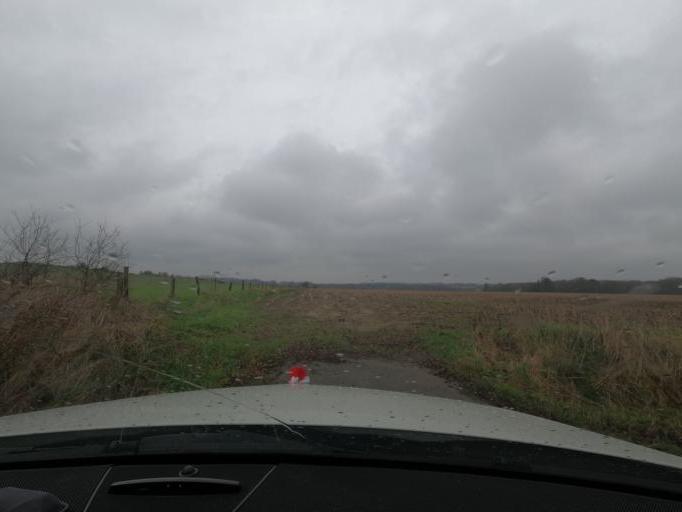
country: DK
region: South Denmark
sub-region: Haderslev Kommune
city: Starup
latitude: 55.2432
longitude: 9.5219
